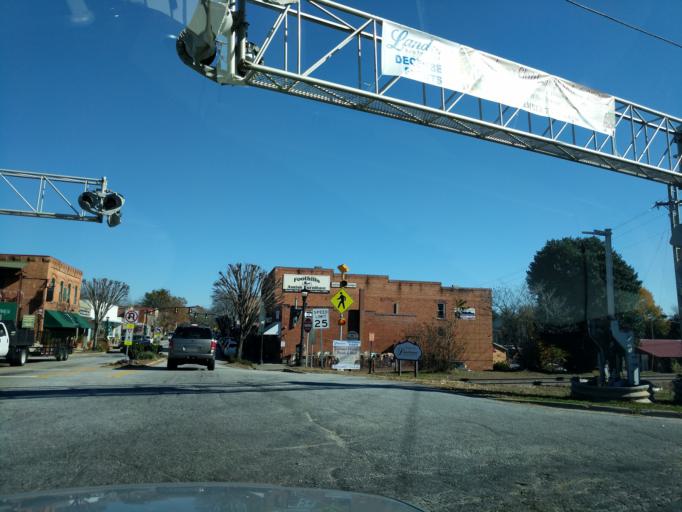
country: US
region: South Carolina
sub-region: Spartanburg County
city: Landrum
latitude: 35.1746
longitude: -82.1899
